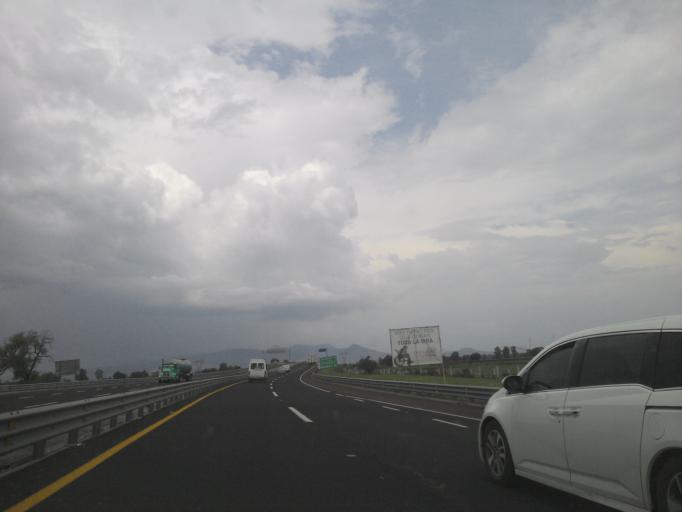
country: MX
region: Hidalgo
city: Doxey
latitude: 20.0987
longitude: -99.2797
